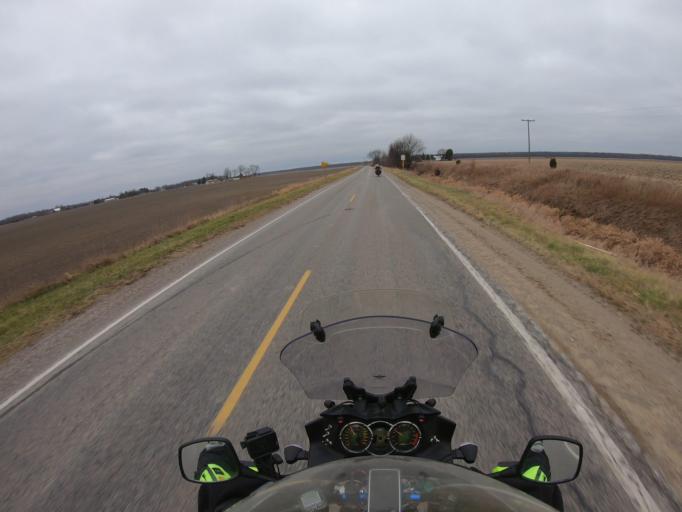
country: US
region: Michigan
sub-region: Saginaw County
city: Saint Charles
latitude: 43.2624
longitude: -84.1097
